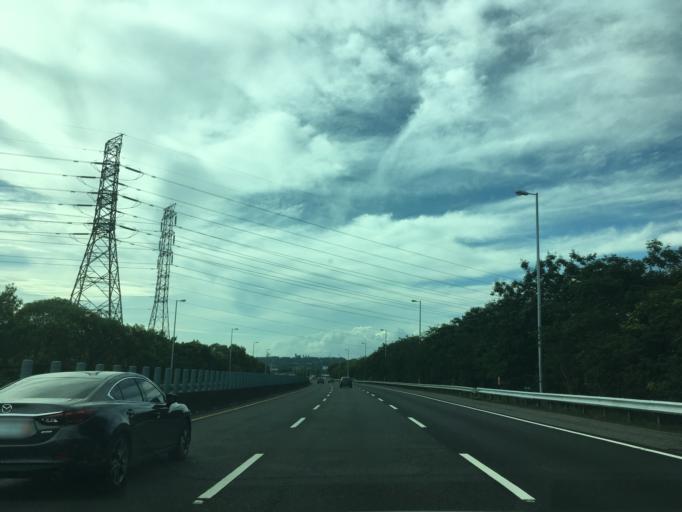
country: TW
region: Taiwan
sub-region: Chiayi
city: Jiayi Shi
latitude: 23.5013
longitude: 120.4924
